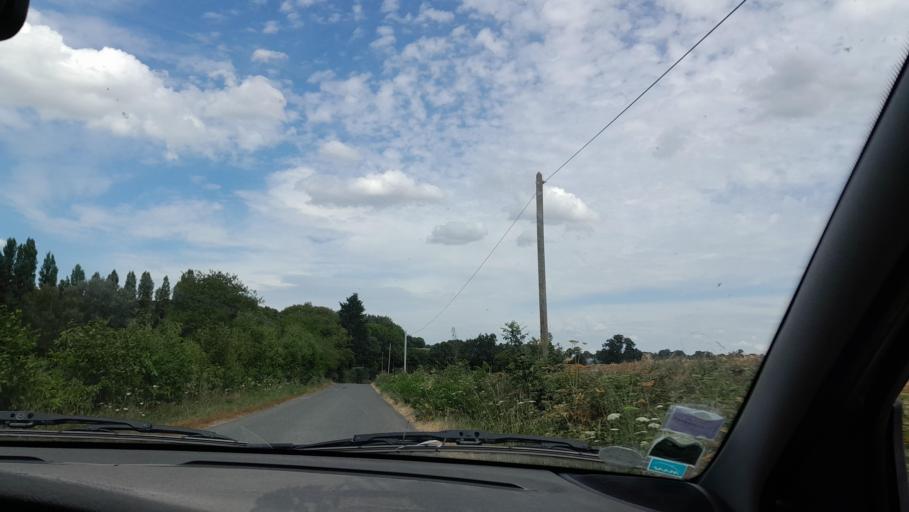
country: FR
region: Pays de la Loire
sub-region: Departement de la Mayenne
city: Juvigne
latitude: 48.1823
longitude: -1.0370
